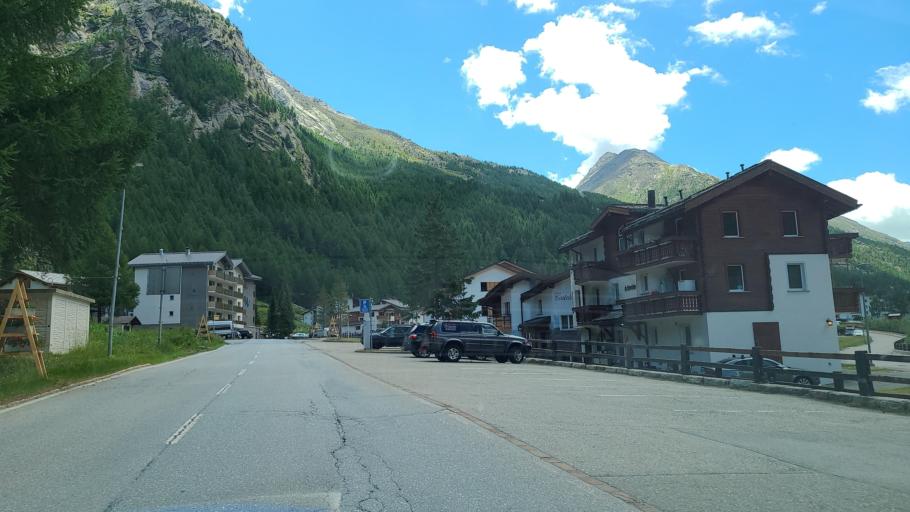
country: CH
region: Valais
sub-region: Visp District
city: Saas-Fee
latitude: 46.0987
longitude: 7.9552
